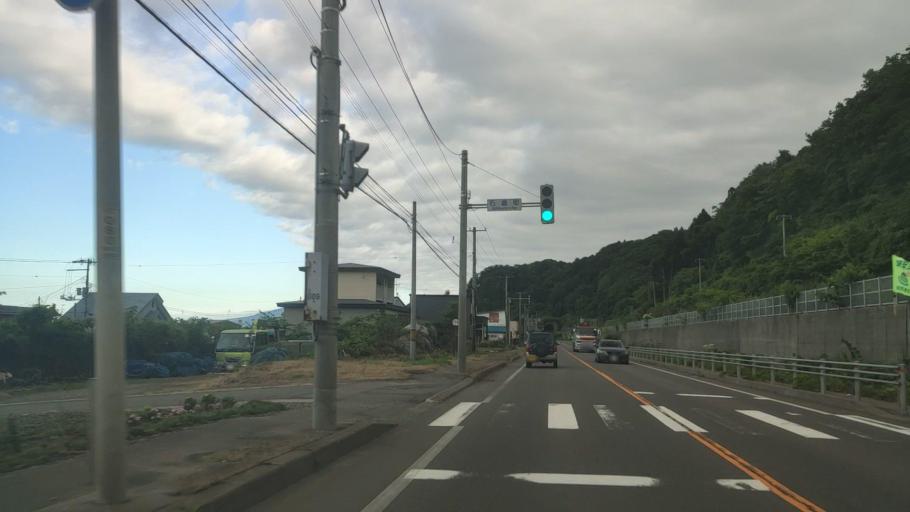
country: JP
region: Hokkaido
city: Nanae
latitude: 42.1600
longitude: 140.4721
